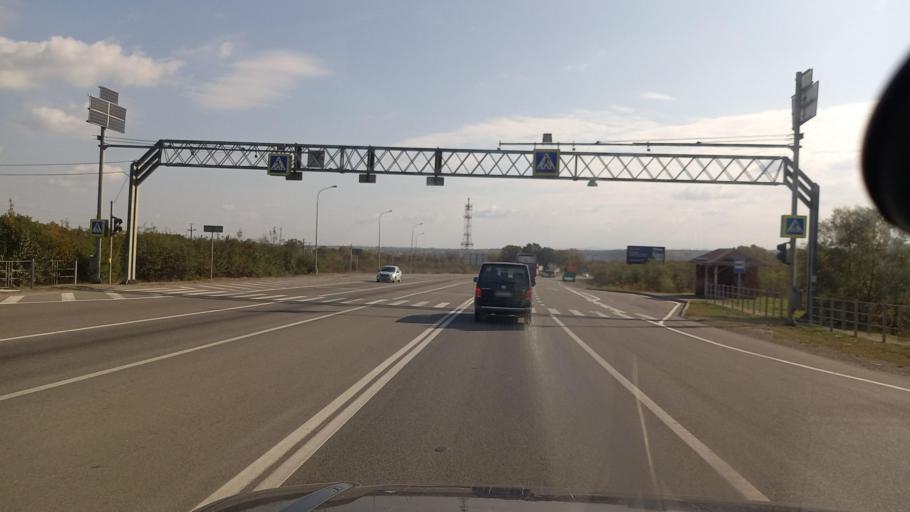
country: RU
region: Krasnodarskiy
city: Abinsk
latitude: 44.8485
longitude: 38.1424
